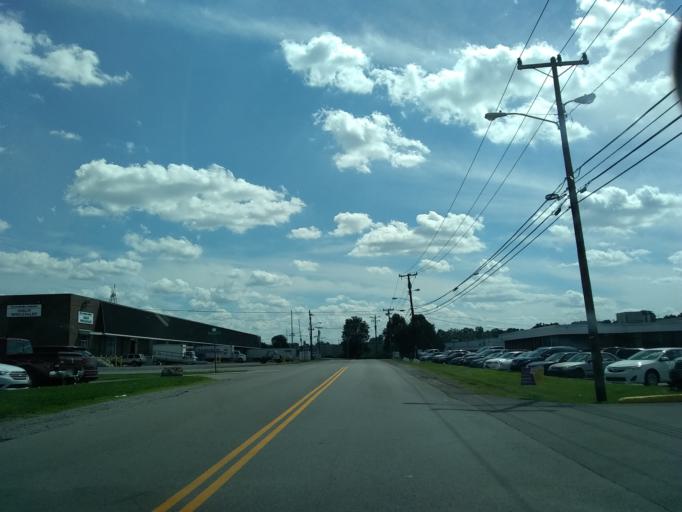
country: US
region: Tennessee
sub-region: Davidson County
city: Nashville
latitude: 36.1511
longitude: -86.7086
